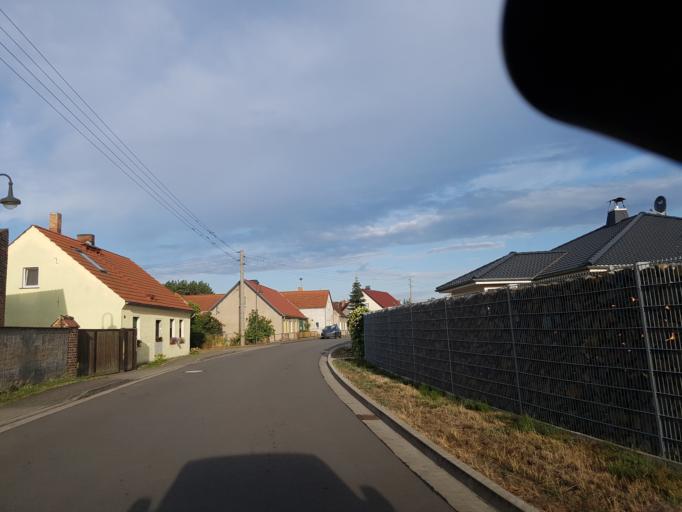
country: DE
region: Saxony-Anhalt
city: Holzdorf
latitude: 51.8039
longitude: 13.0853
